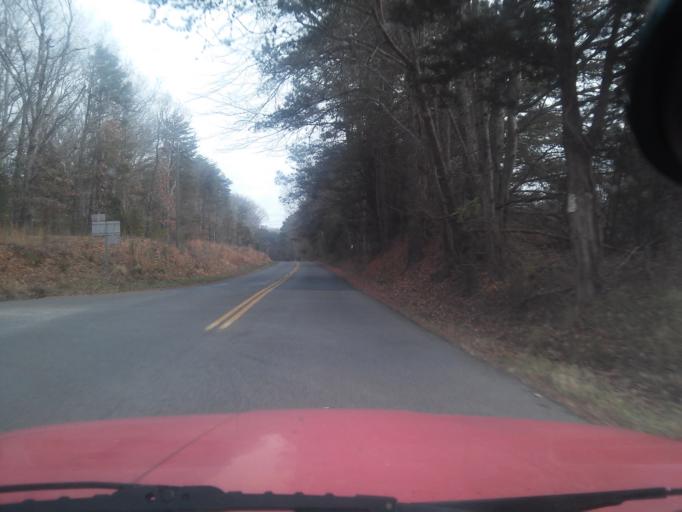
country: US
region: Virginia
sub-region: Goochland County
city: Goochland
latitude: 37.7156
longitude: -77.7734
